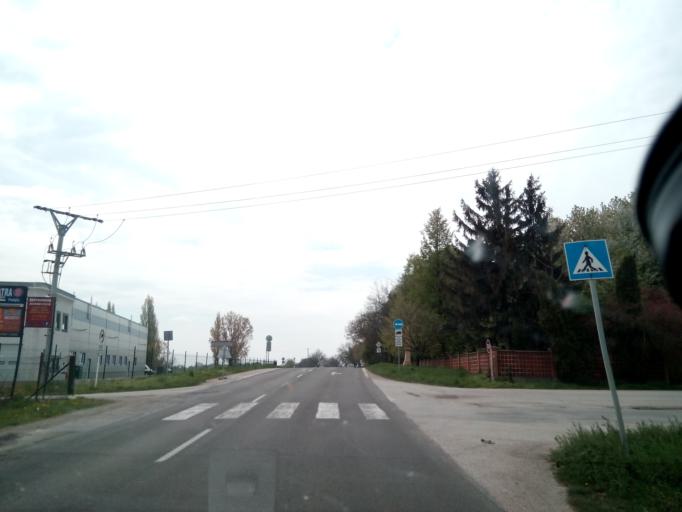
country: SK
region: Trnavsky
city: Vrbove
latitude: 48.5943
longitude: 17.7482
